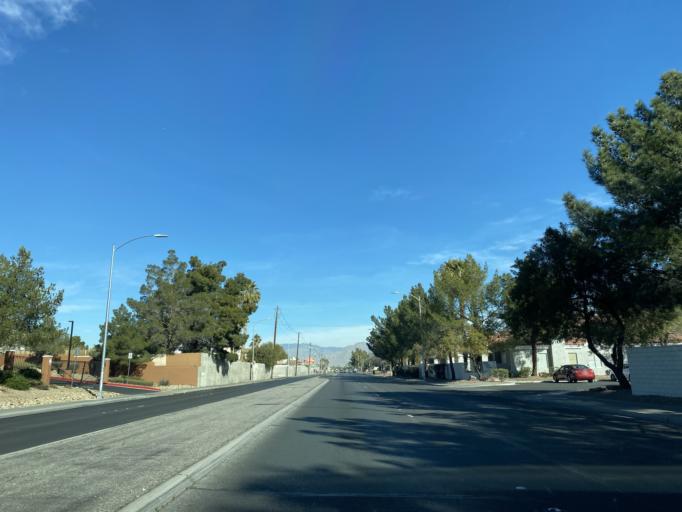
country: US
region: Nevada
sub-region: Clark County
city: Spring Valley
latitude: 36.1911
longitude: -115.2240
